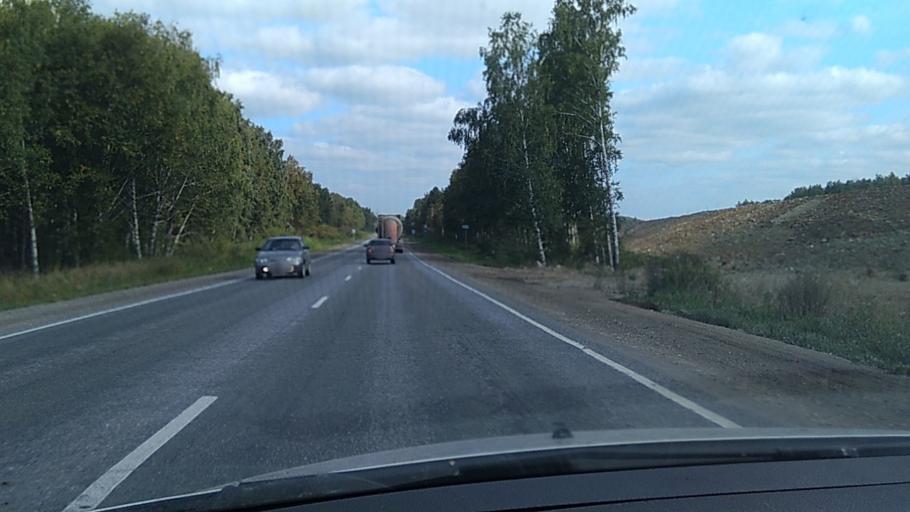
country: RU
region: Chelyabinsk
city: Chebarkul'
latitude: 54.9224
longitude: 60.2913
